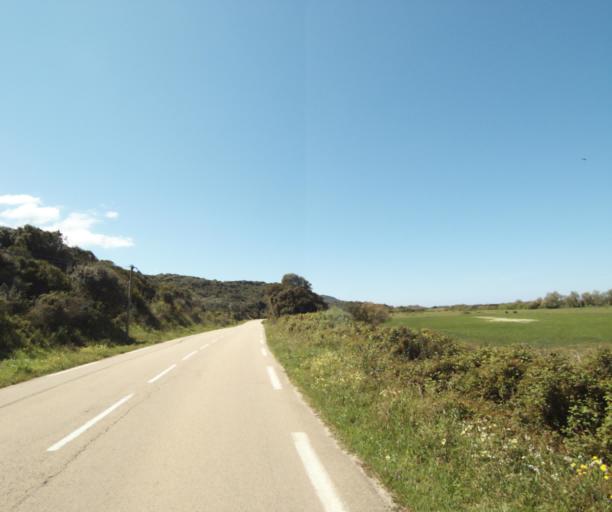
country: FR
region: Corsica
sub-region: Departement de la Corse-du-Sud
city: Propriano
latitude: 41.6543
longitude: 8.8913
